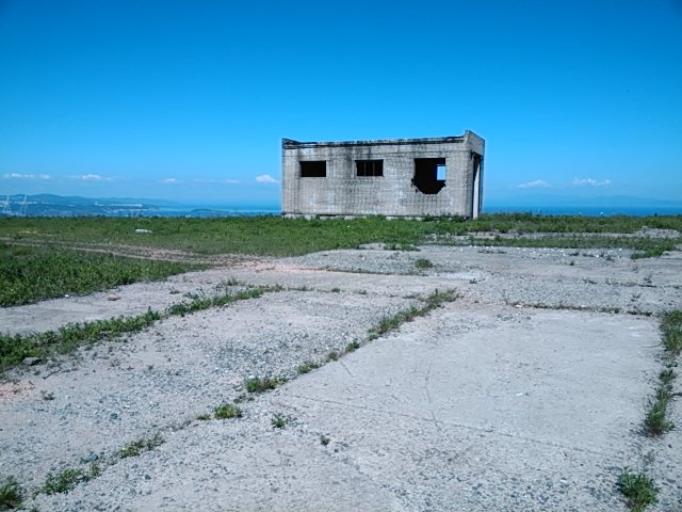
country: RU
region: Primorskiy
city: Russkiy
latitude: 42.9892
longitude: 131.8338
